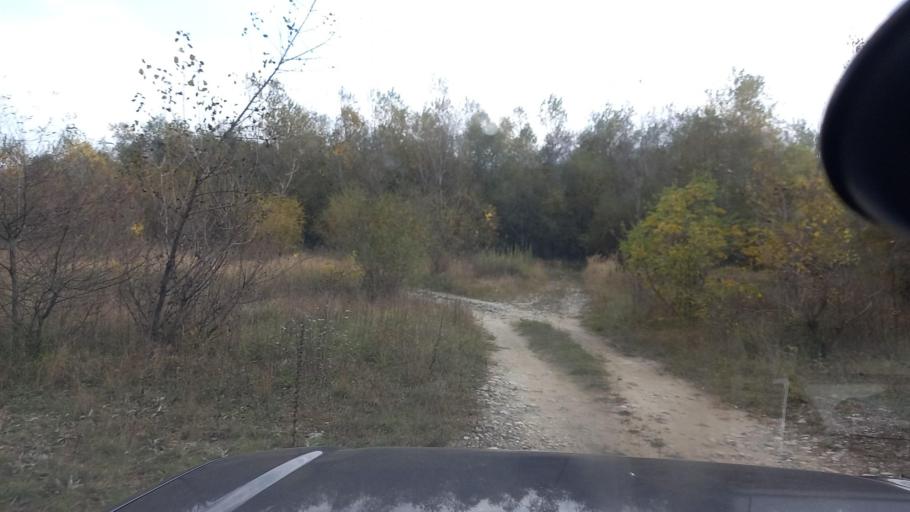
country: RU
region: Krasnodarskiy
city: Shedok
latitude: 44.1698
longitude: 40.8475
